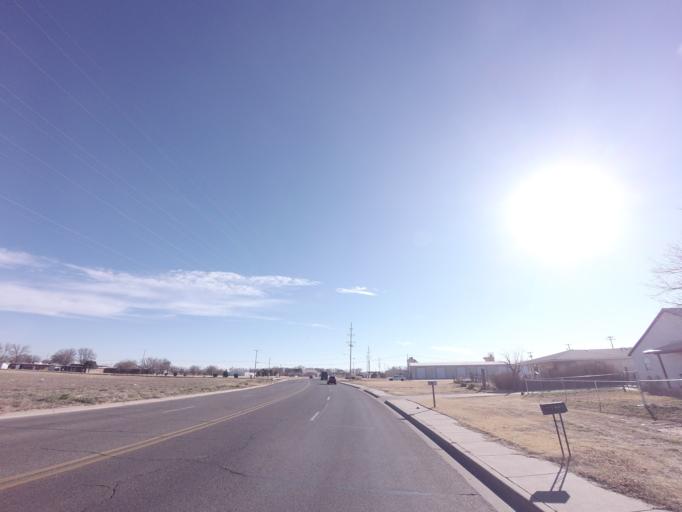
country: US
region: New Mexico
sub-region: Curry County
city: Clovis
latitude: 34.4006
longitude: -103.1789
